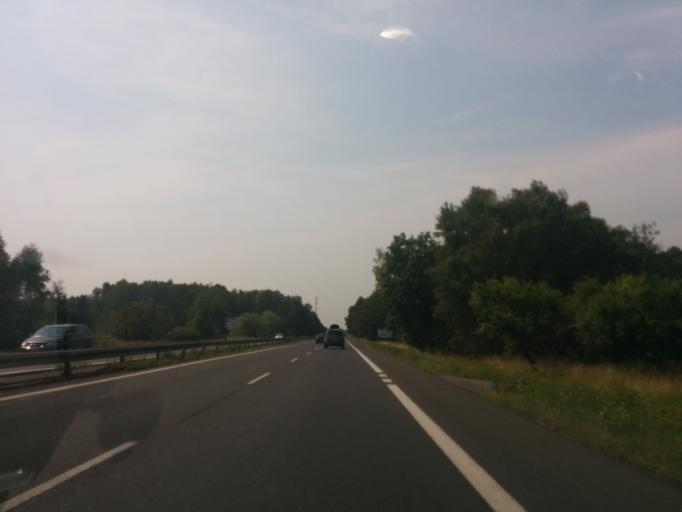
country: PL
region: Lodz Voivodeship
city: Zabia Wola
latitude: 52.0327
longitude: 20.6835
